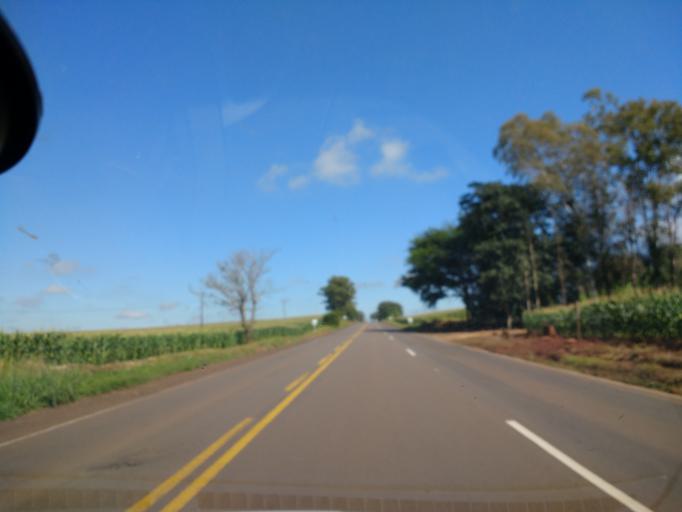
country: BR
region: Parana
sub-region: Terra Boa
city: Terra Boa
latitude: -23.5997
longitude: -52.3972
